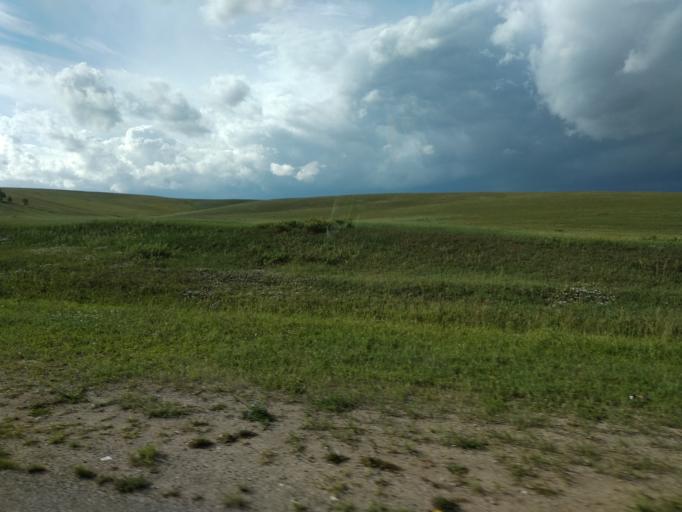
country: RU
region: Irkutsk
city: Bayanday
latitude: 52.9708
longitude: 105.3566
